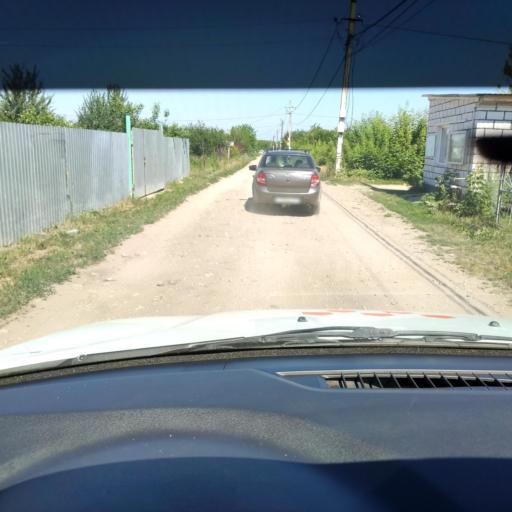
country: RU
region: Samara
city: Tol'yatti
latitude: 53.5682
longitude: 49.3719
